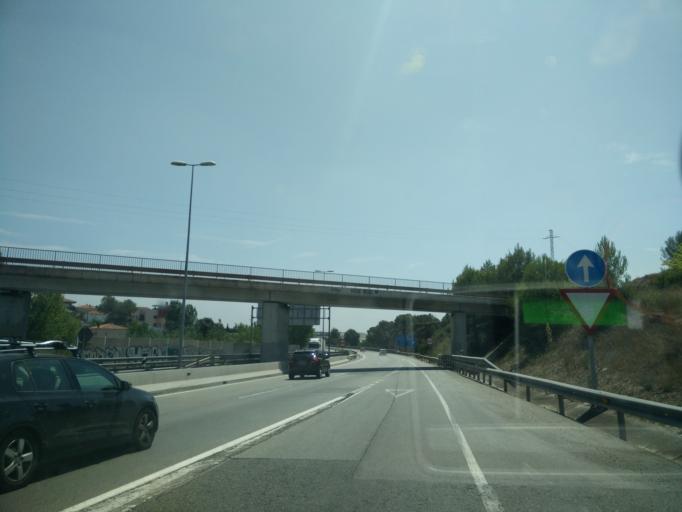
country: ES
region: Catalonia
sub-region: Provincia de Barcelona
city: Esparreguera
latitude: 41.5323
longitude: 1.8659
